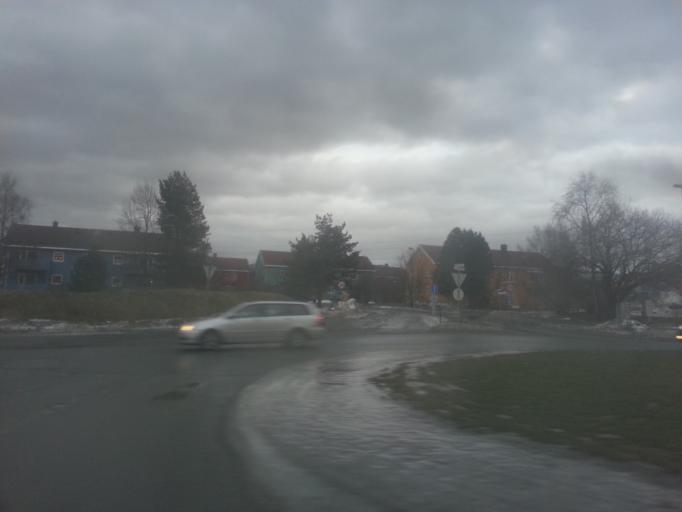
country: NO
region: Sor-Trondelag
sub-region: Trondheim
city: Trondheim
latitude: 63.4303
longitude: 10.4546
